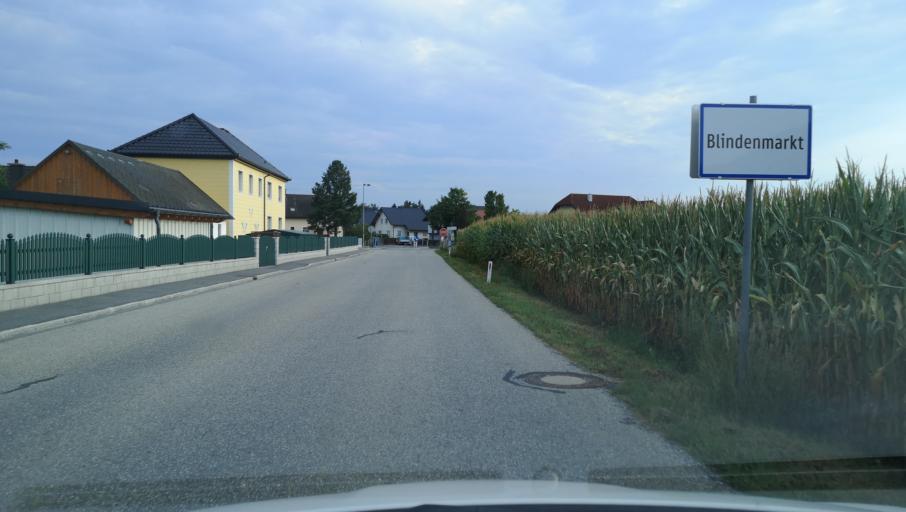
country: AT
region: Lower Austria
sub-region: Politischer Bezirk Melk
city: Blindenmarkt
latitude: 48.1303
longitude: 14.9796
